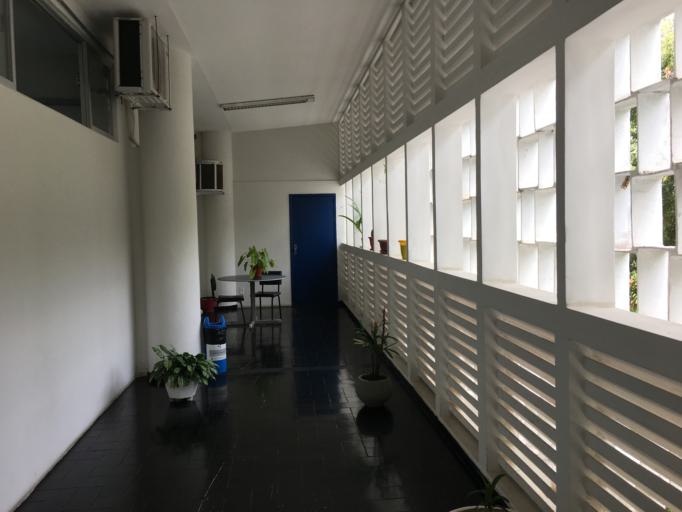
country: BR
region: Bahia
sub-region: Salvador
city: Salvador
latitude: -12.9997
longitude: -38.5106
